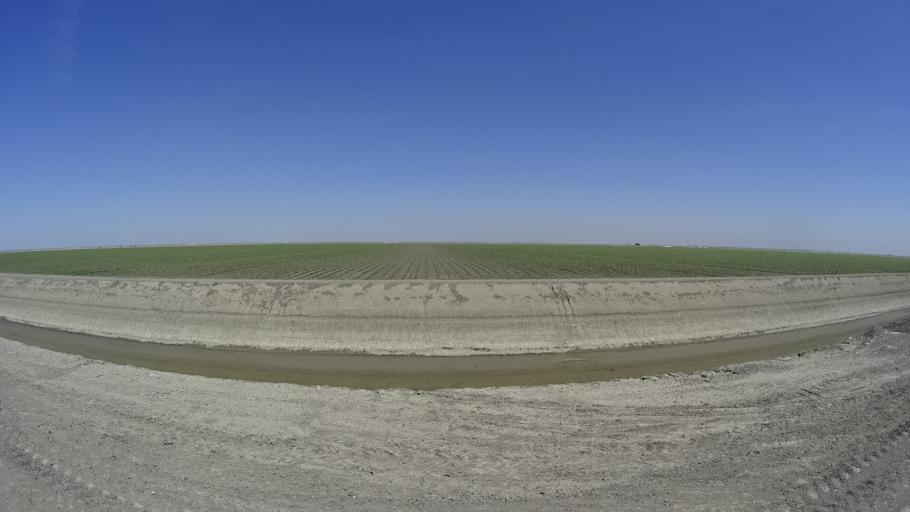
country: US
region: California
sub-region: Kings County
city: Corcoran
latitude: 36.0214
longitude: -119.6578
